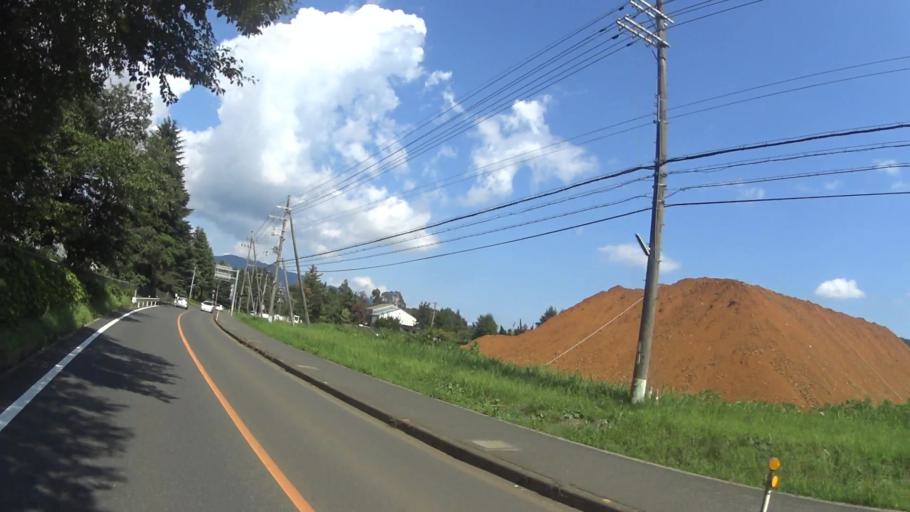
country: JP
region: Kyoto
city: Miyazu
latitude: 35.5553
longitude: 135.1513
